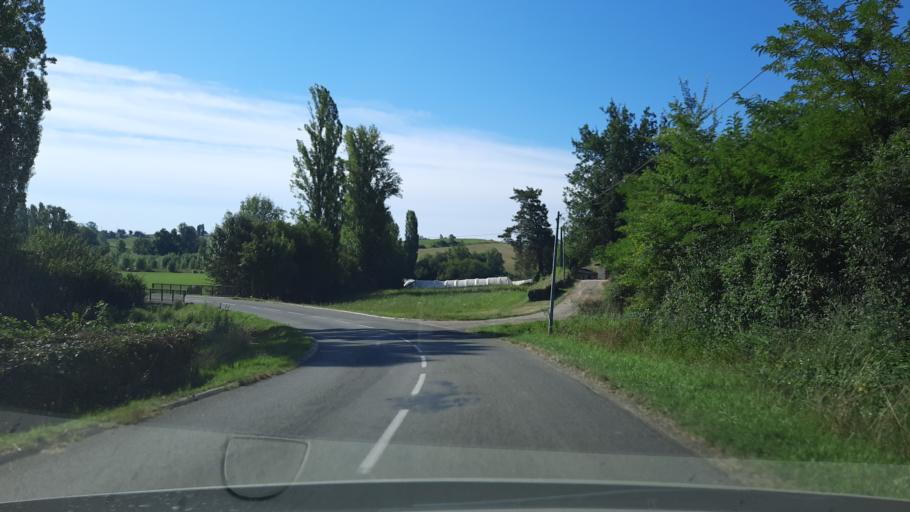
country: FR
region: Midi-Pyrenees
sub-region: Departement du Tarn-et-Garonne
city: Molieres
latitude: 44.1986
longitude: 1.4290
